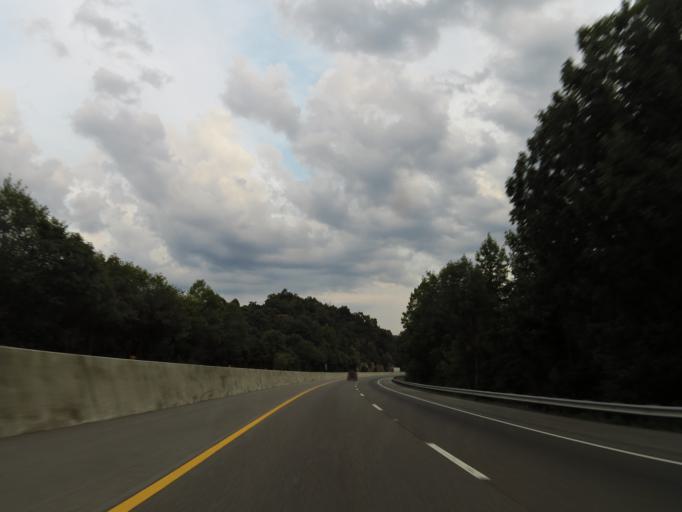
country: US
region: Tennessee
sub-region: Anderson County
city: Norris
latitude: 36.1152
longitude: -84.0274
